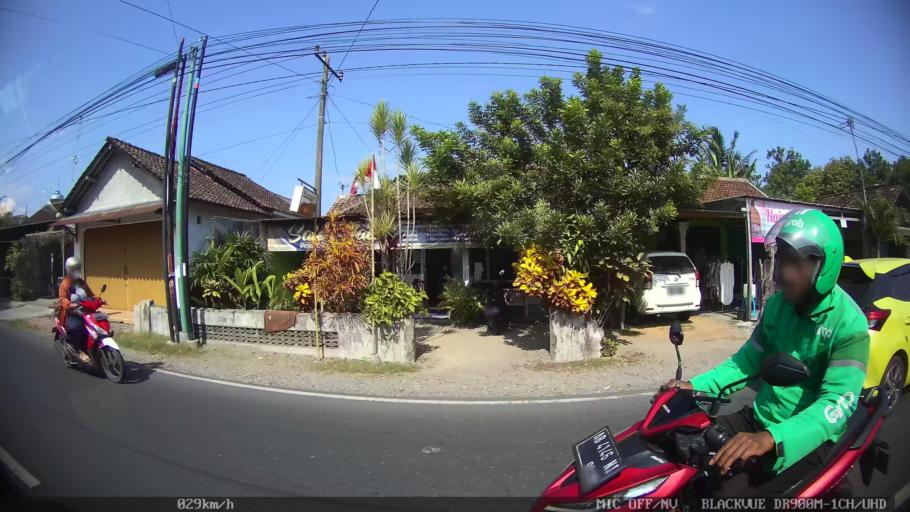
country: ID
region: Daerah Istimewa Yogyakarta
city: Sewon
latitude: -7.8818
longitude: 110.3894
